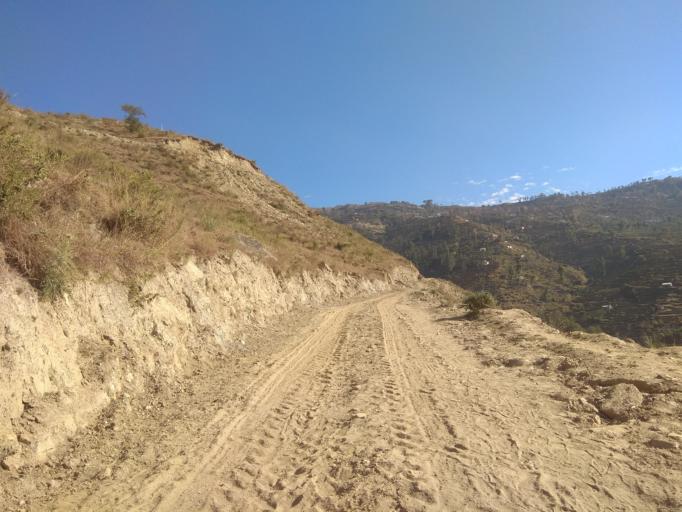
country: NP
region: Far Western
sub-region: Seti Zone
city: Achham
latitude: 29.2461
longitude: 81.6269
